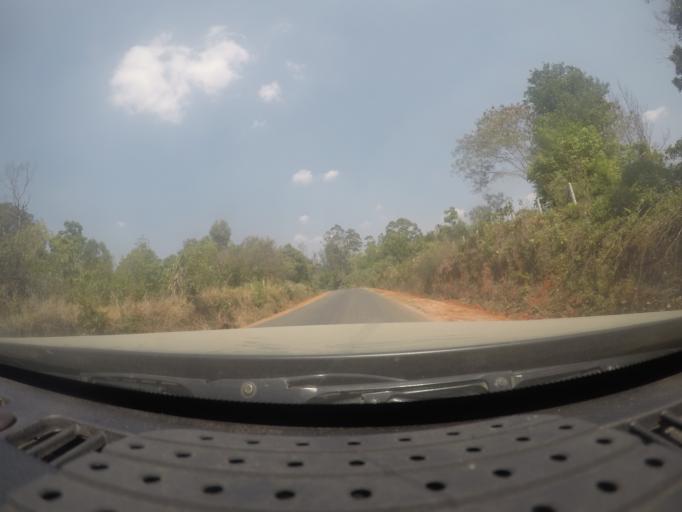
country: MM
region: Shan
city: Taunggyi
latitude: 21.0431
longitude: 96.5129
